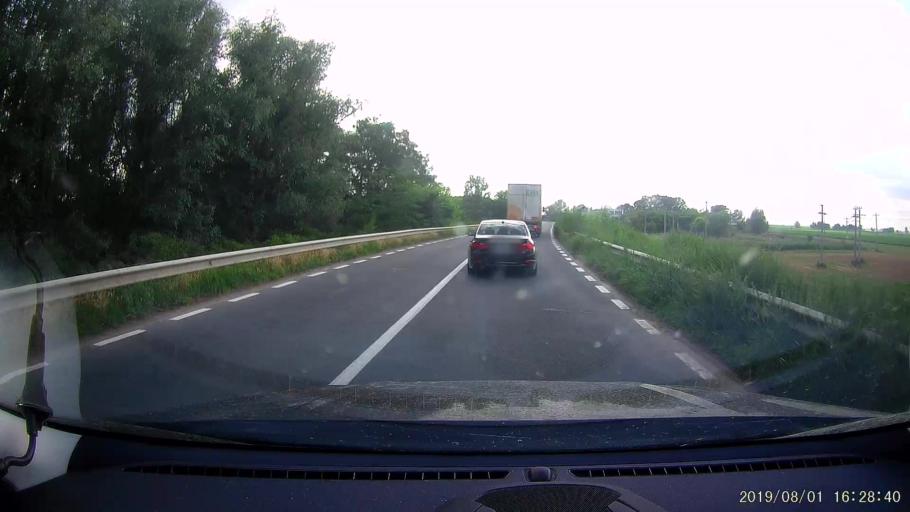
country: BG
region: Silistra
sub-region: Obshtina Silistra
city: Silistra
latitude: 44.1459
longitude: 27.3044
